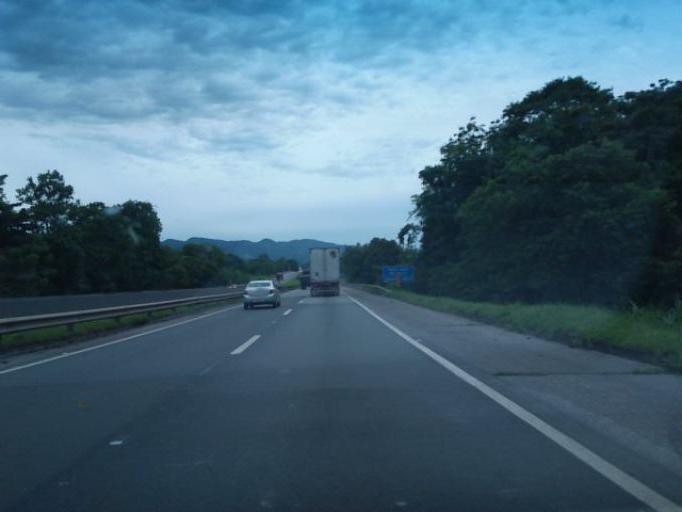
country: BR
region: Sao Paulo
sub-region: Miracatu
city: Miracatu
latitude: -24.2431
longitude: -47.3651
